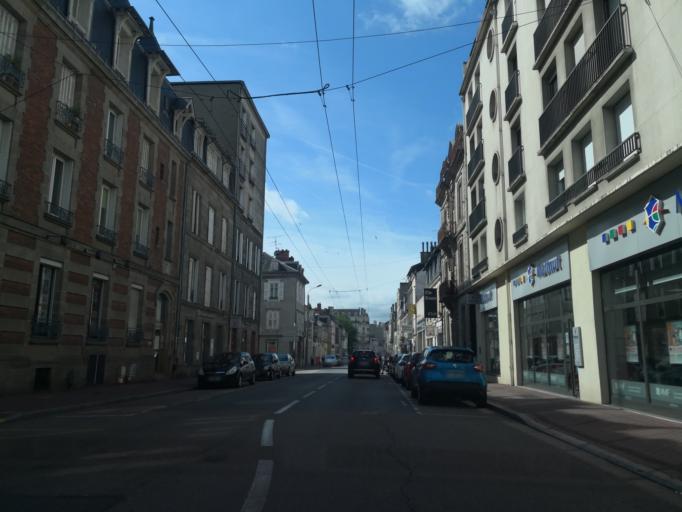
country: FR
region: Limousin
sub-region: Departement de la Haute-Vienne
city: Limoges
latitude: 45.8343
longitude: 1.2609
